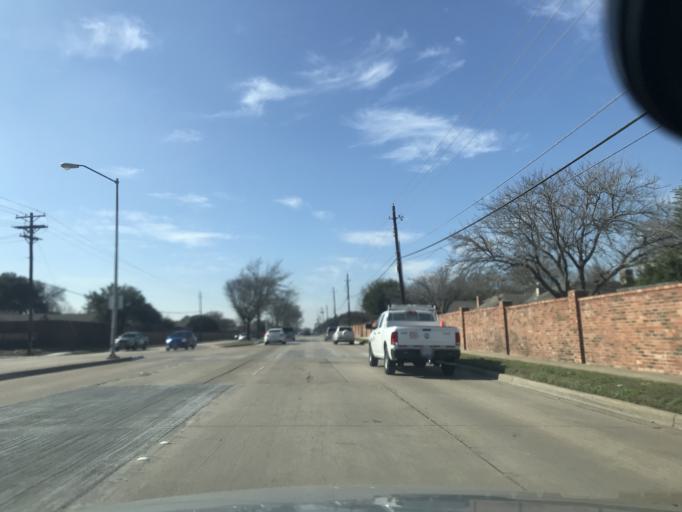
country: US
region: Texas
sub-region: Collin County
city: Plano
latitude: 33.0411
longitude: -96.7259
